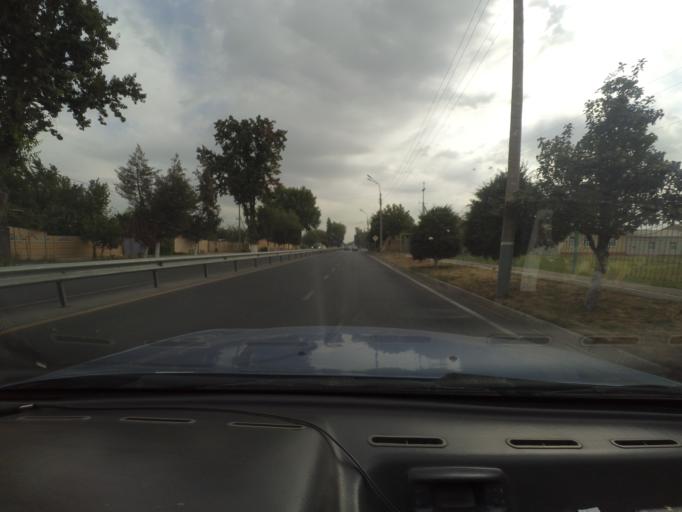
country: UZ
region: Toshkent
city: Qibray
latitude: 41.3831
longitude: 69.4484
